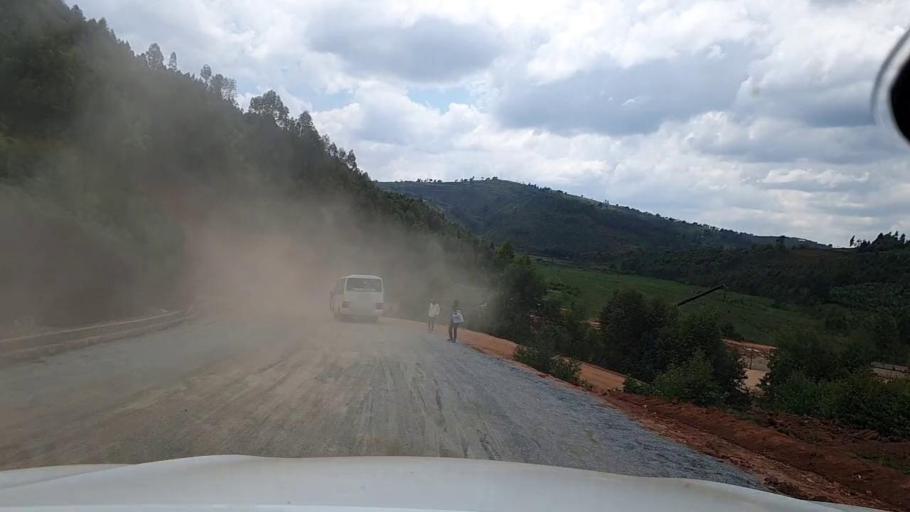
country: RW
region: Southern Province
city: Butare
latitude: -2.6961
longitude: 29.5549
